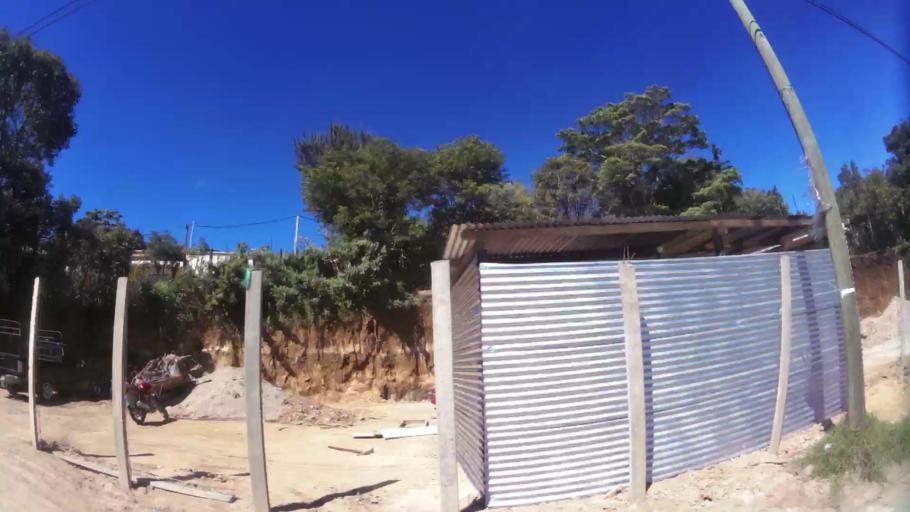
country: GT
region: Guatemala
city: San Jose Pinula
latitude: 14.5250
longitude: -90.4166
